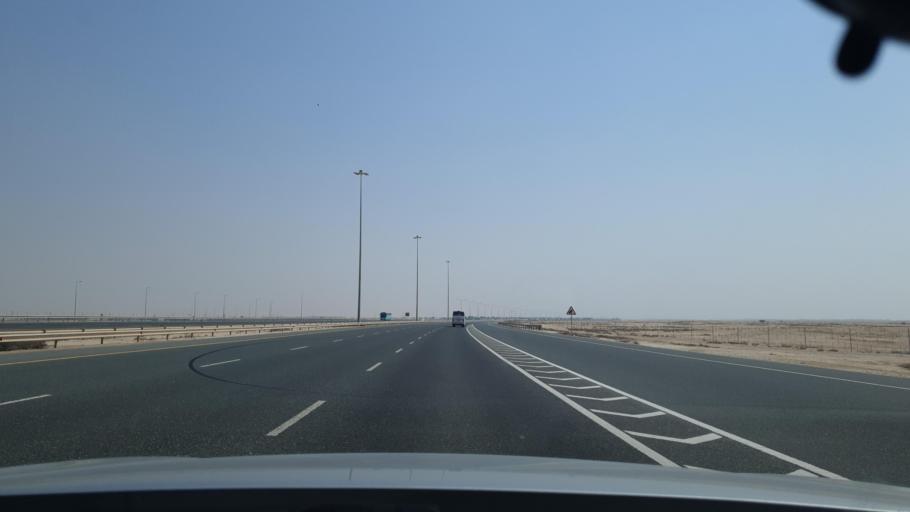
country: QA
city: Al Ghuwayriyah
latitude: 25.8269
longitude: 51.3557
